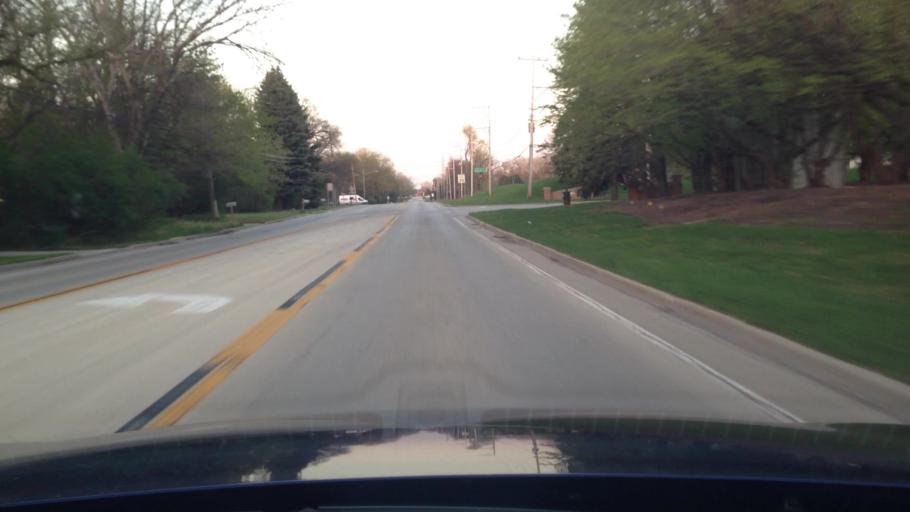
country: US
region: Illinois
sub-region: Cook County
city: Prospect Heights
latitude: 42.0952
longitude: -87.9230
